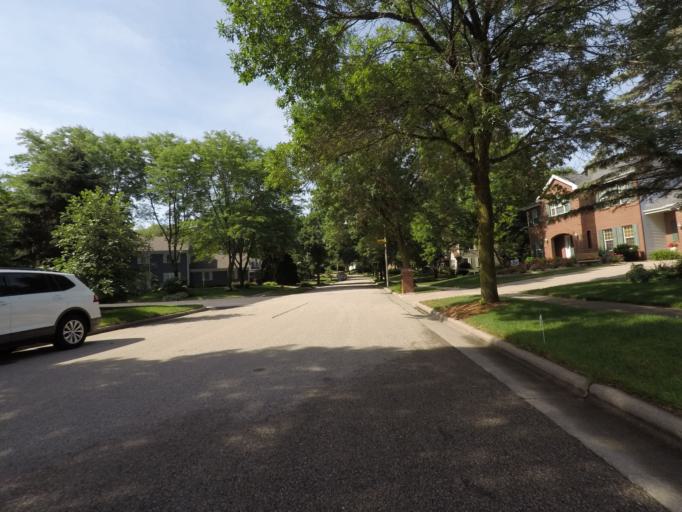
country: US
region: Wisconsin
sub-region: Dane County
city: Middleton
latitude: 43.0814
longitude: -89.4938
